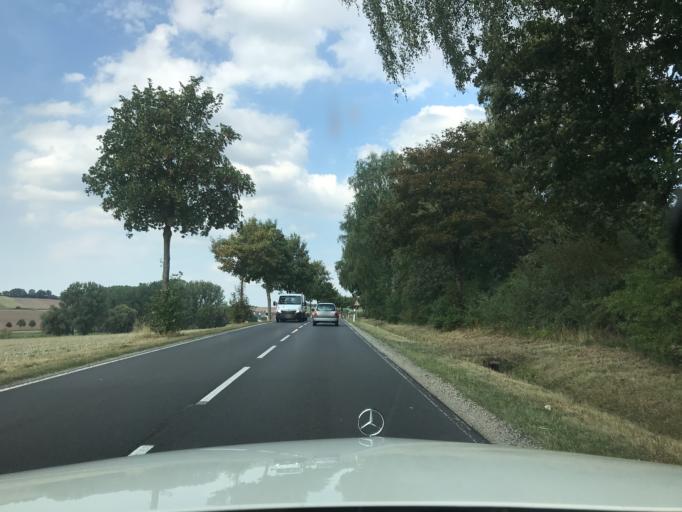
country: DE
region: Lower Saxony
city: Adelebsen
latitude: 51.5918
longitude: 9.7688
